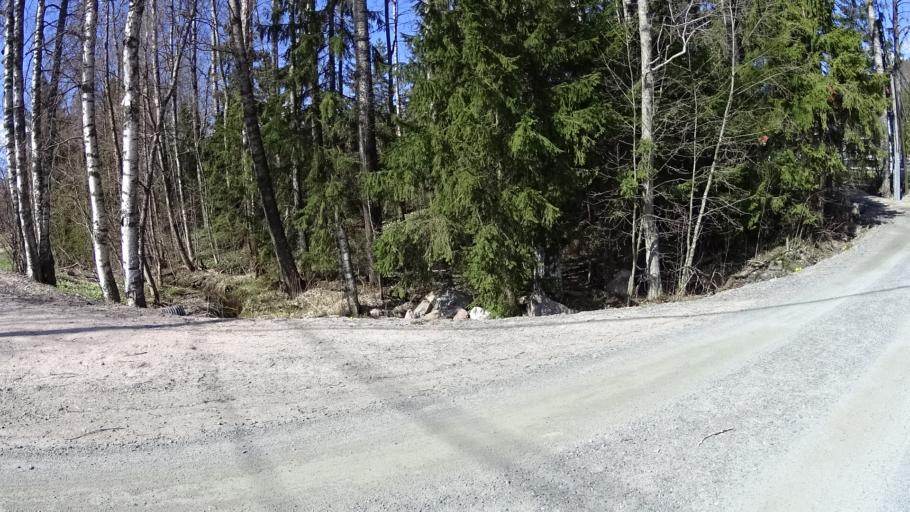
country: FI
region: Uusimaa
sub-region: Helsinki
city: Espoo
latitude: 60.2369
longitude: 24.6452
